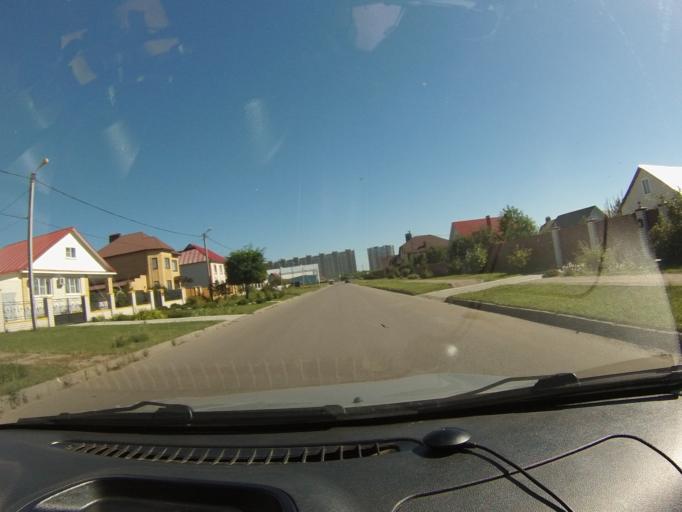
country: RU
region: Tambov
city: Tambov
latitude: 52.7683
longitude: 41.3865
